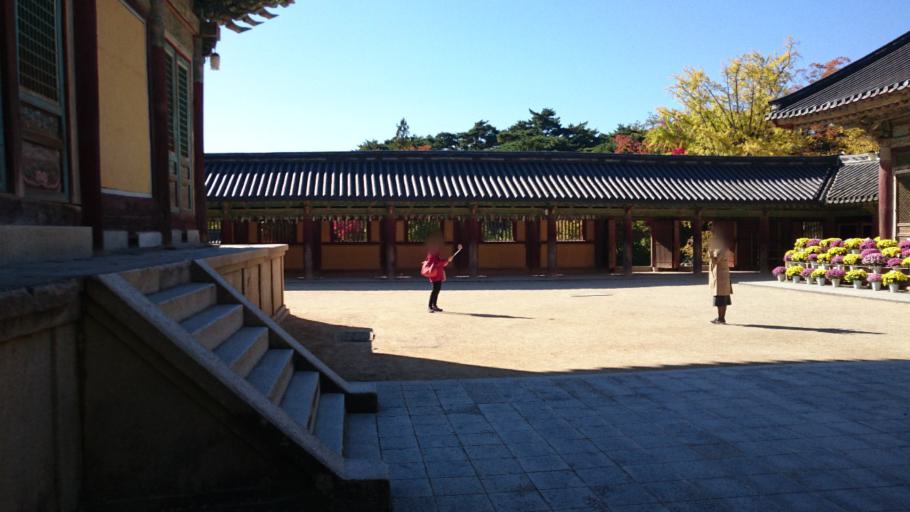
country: KR
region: Gyeongsangbuk-do
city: Kyonju
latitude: 35.7902
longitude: 129.3322
